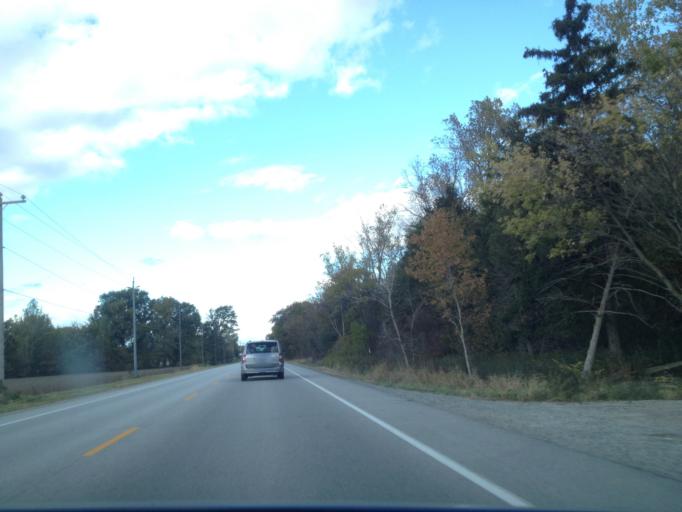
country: CA
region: Ontario
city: Amherstburg
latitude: 42.0849
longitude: -82.7361
